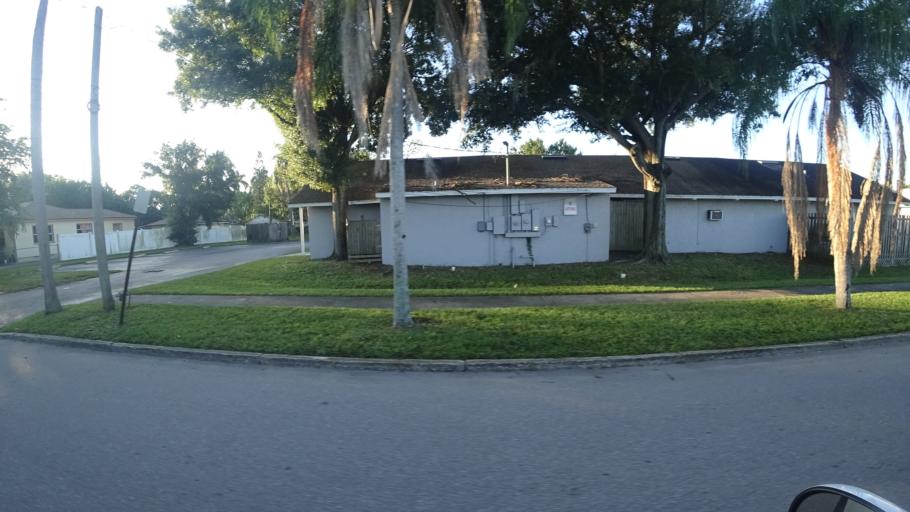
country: US
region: Florida
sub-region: Manatee County
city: Bradenton
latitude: 27.4817
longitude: -82.5708
